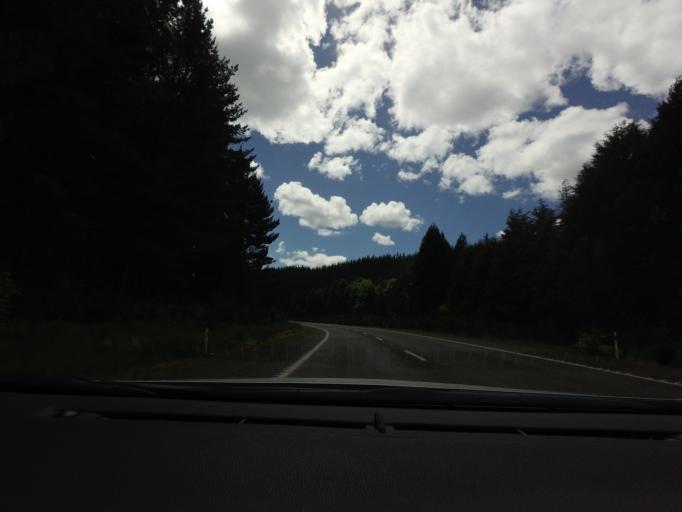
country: NZ
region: Bay of Plenty
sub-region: Rotorua District
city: Rotorua
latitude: -38.2298
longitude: 176.2976
